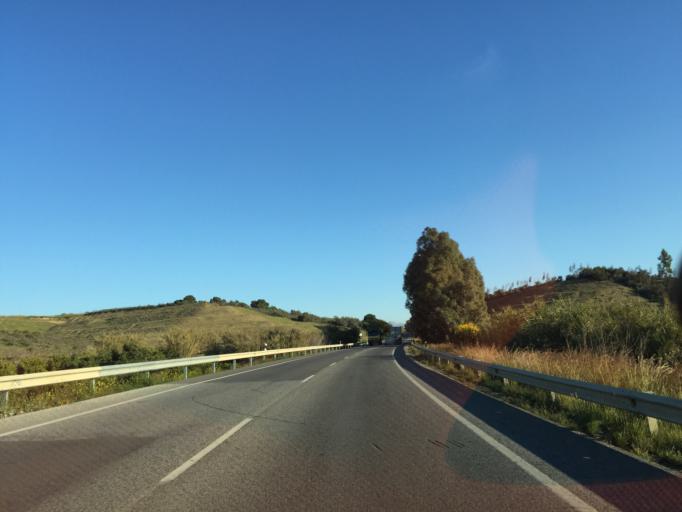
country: ES
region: Andalusia
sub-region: Provincia de Malaga
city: Pizarra
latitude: 36.7252
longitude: -4.7092
